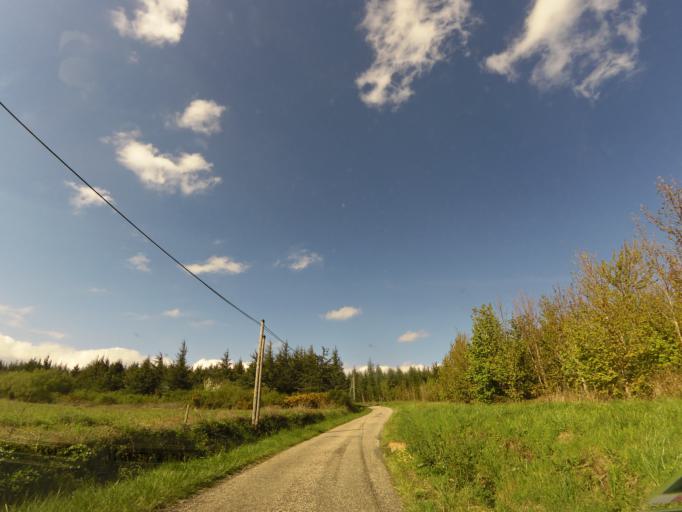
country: FR
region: Midi-Pyrenees
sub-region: Departement du Tarn
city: Soreze
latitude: 43.3778
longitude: 2.0670
